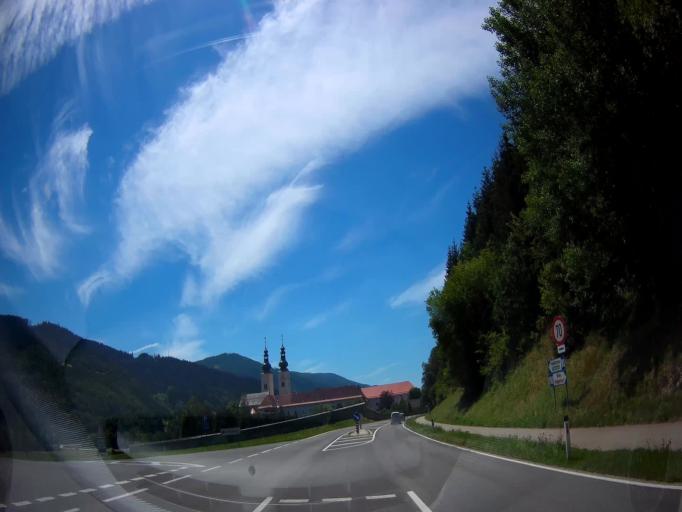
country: AT
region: Carinthia
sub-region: Politischer Bezirk Sankt Veit an der Glan
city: Gurk
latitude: 46.8772
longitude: 14.2962
